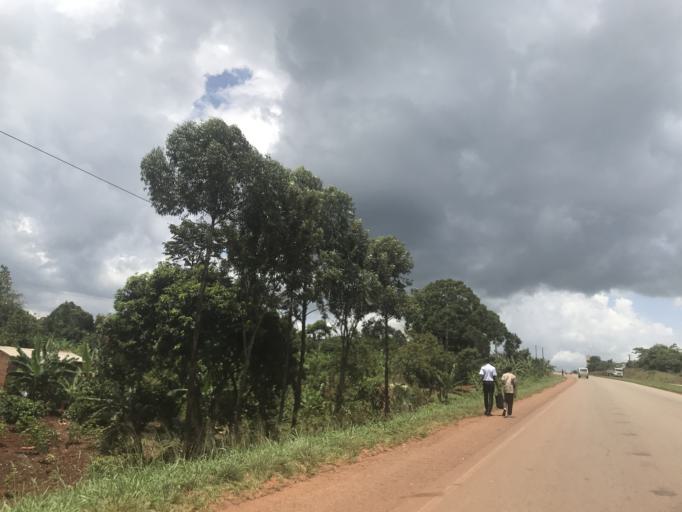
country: UG
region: Eastern Region
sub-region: Jinja District
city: Bugembe
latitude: 0.4772
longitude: 33.2675
